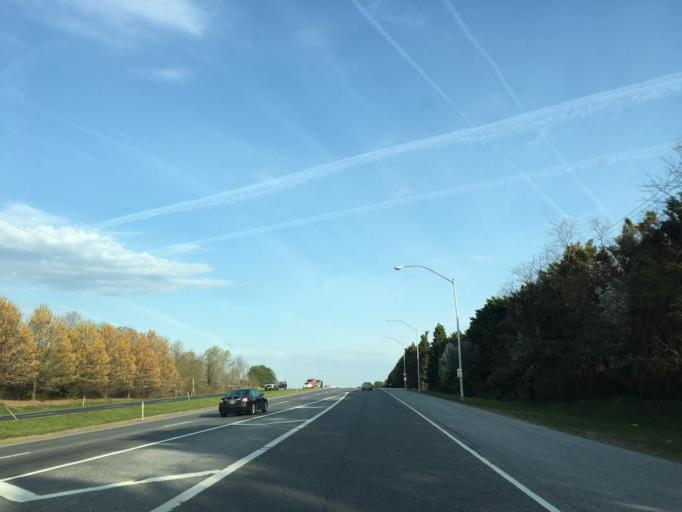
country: US
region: Maryland
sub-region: Baltimore County
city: Reisterstown
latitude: 39.4749
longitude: -76.8401
